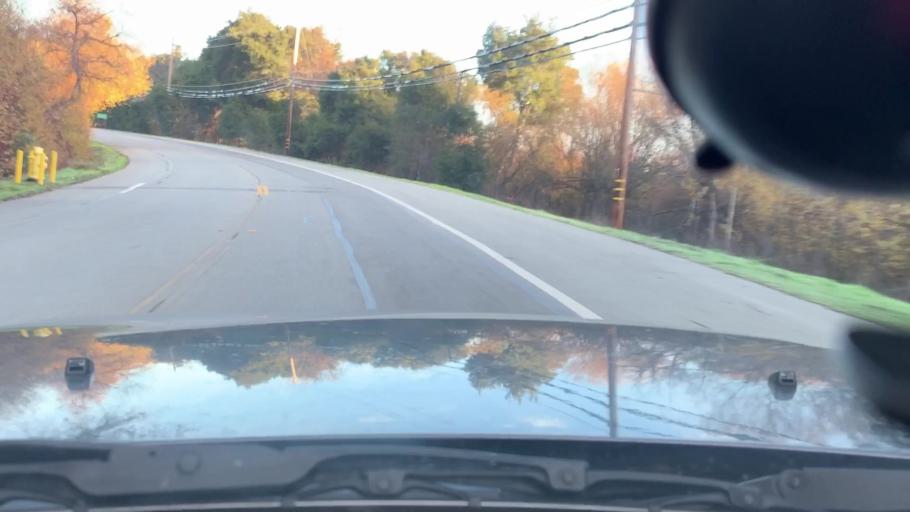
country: US
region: California
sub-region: San Mateo County
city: Portola Valley
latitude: 37.3986
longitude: -122.2443
